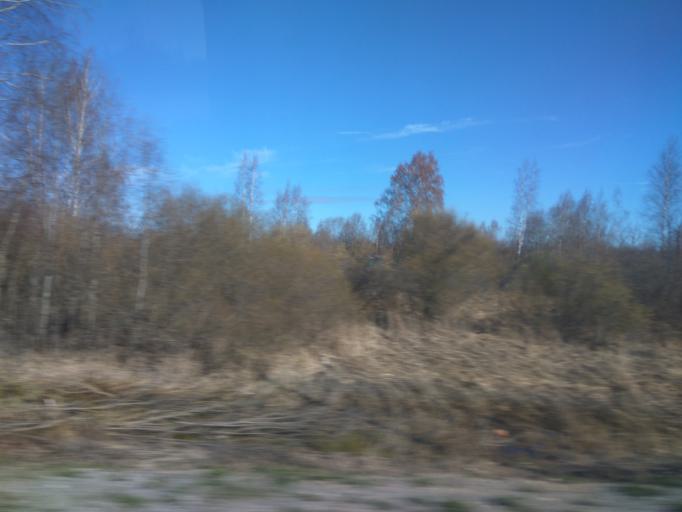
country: RU
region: Pskov
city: Izborsk
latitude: 57.7162
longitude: 27.9170
